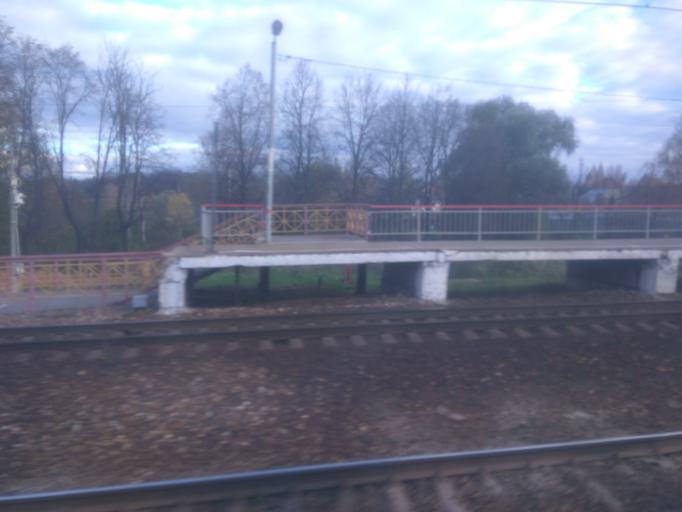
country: RU
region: Moskovskaya
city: Lesnoy Gorodok
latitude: 55.6324
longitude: 37.2185
